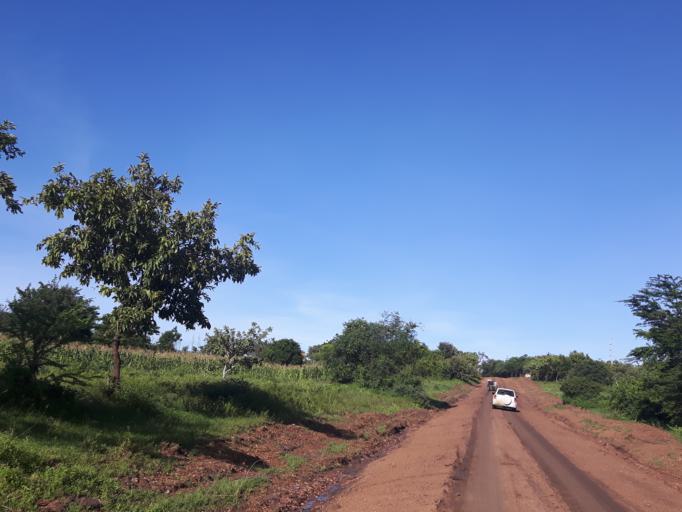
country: TZ
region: Mara
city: Mugumu
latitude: -1.9017
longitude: 34.5974
